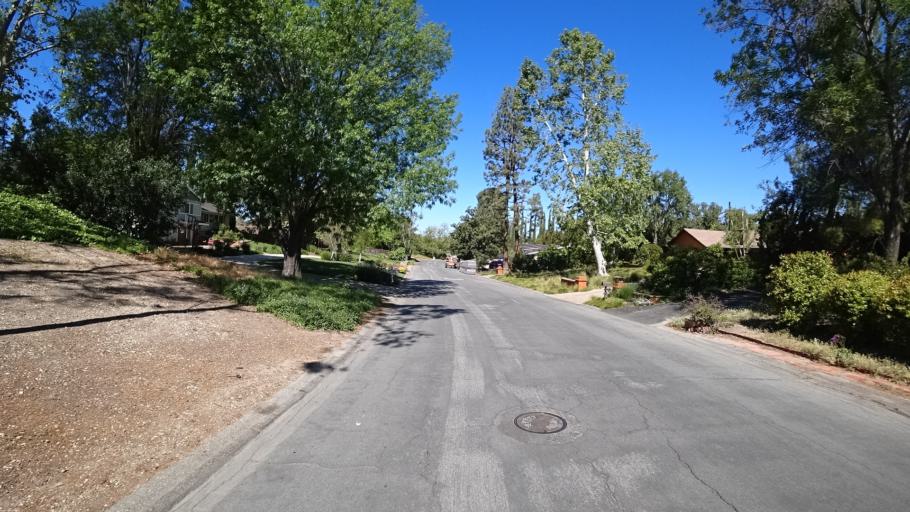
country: US
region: California
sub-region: Ventura County
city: Thousand Oaks
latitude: 34.1945
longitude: -118.8536
